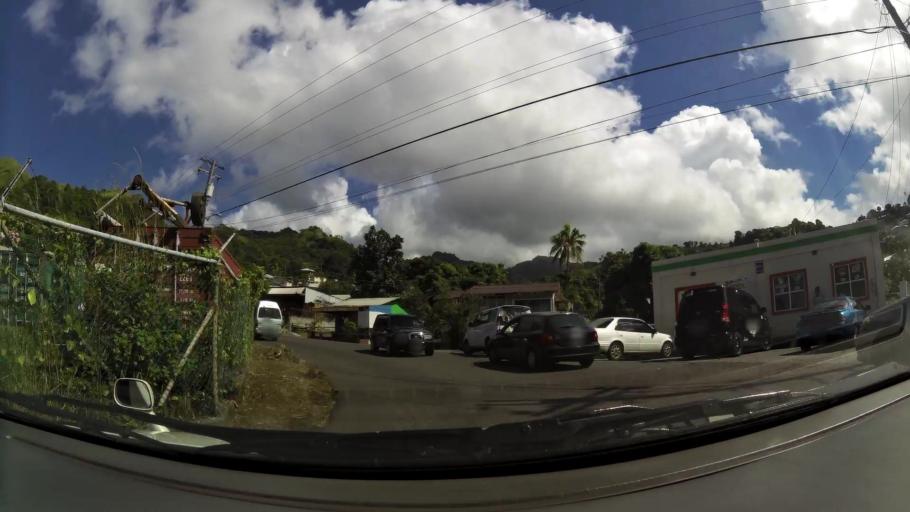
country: VC
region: Saint George
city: Kingstown Park
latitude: 13.1720
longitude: -61.2408
